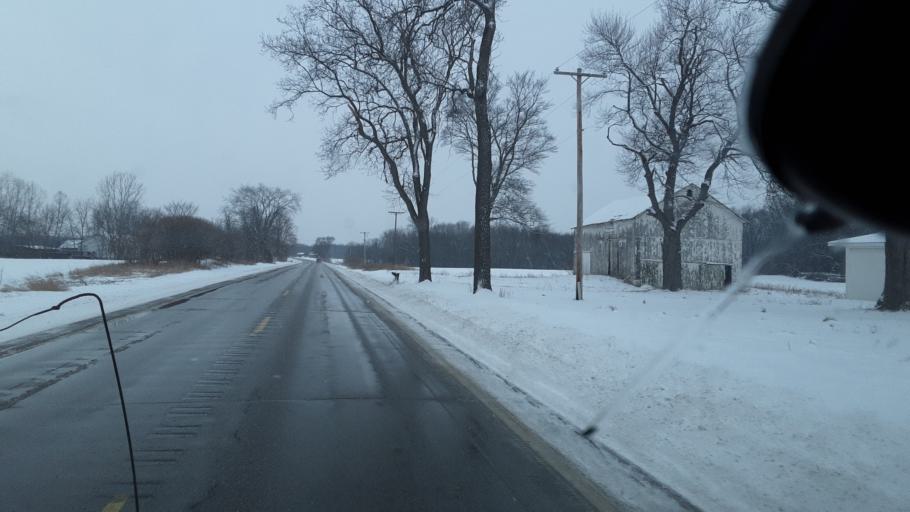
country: US
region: Michigan
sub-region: Jackson County
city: Michigan Center
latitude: 42.3481
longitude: -84.3397
